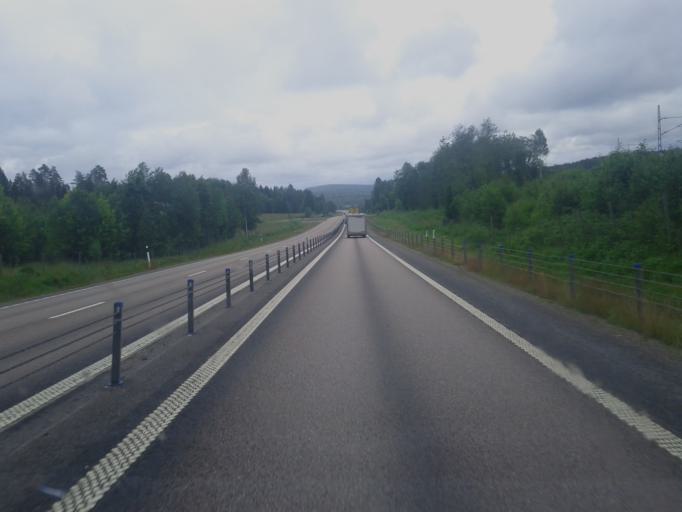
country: SE
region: Vaesternorrland
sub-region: Timra Kommun
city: Soraker
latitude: 62.5503
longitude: 17.6150
